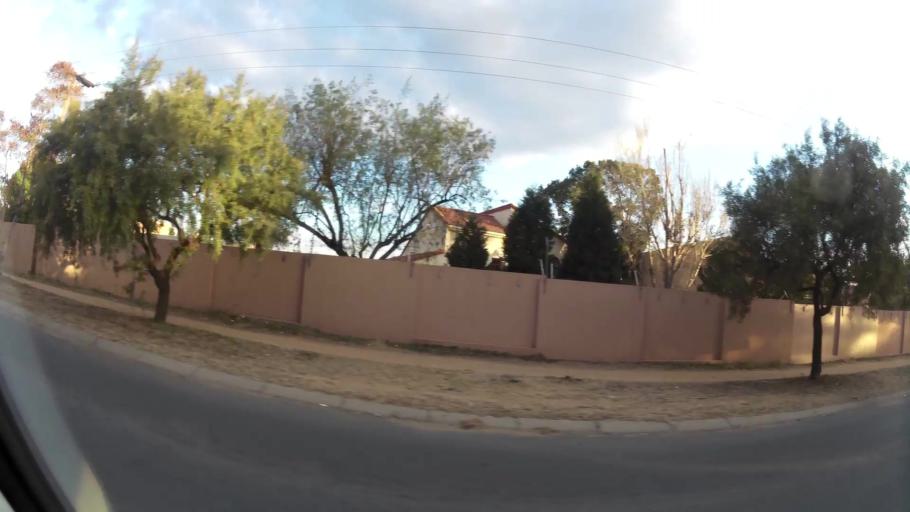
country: ZA
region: Gauteng
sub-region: City of Johannesburg Metropolitan Municipality
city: Diepsloot
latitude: -26.0181
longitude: 27.9954
